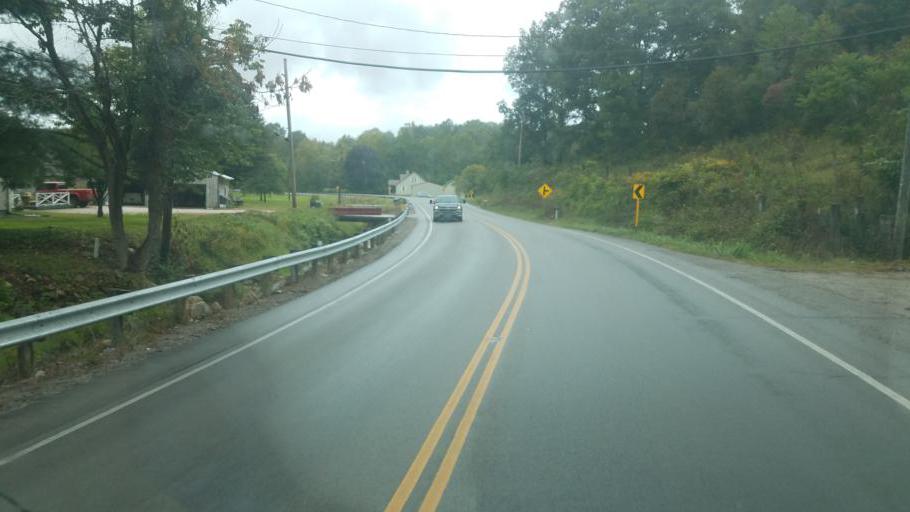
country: US
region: Ohio
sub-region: Scioto County
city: Sciotodale
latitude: 38.7656
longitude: -82.8242
